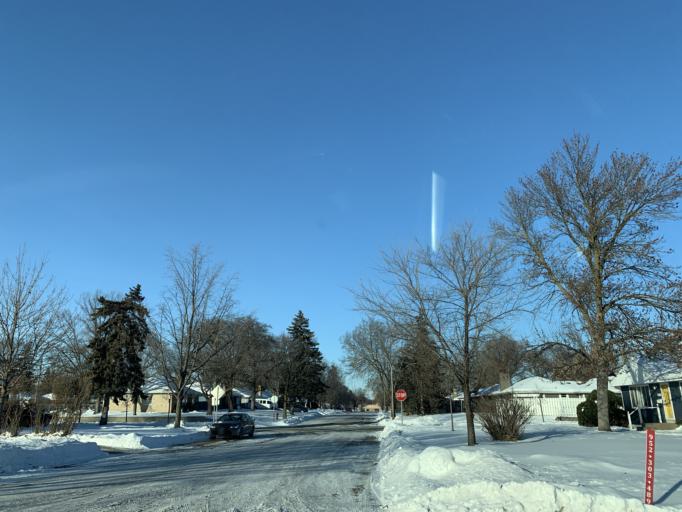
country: US
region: Minnesota
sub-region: Hennepin County
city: Richfield
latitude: 44.8651
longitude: -93.2517
